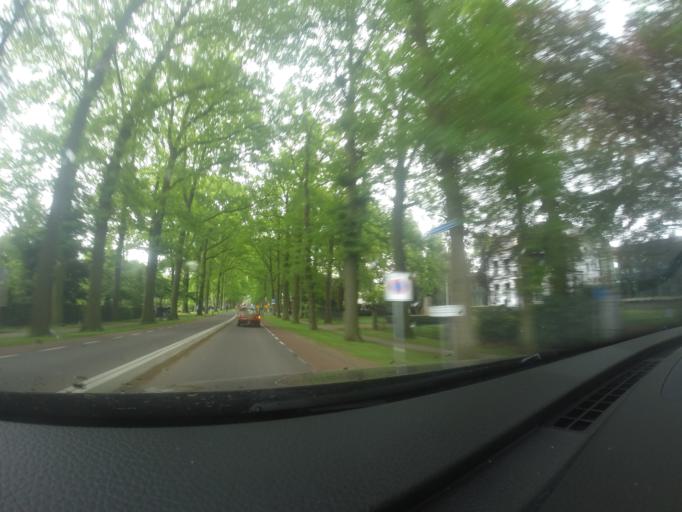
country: NL
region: Gelderland
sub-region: Gemeente Brummen
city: Brummen
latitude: 52.0888
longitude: 6.1466
